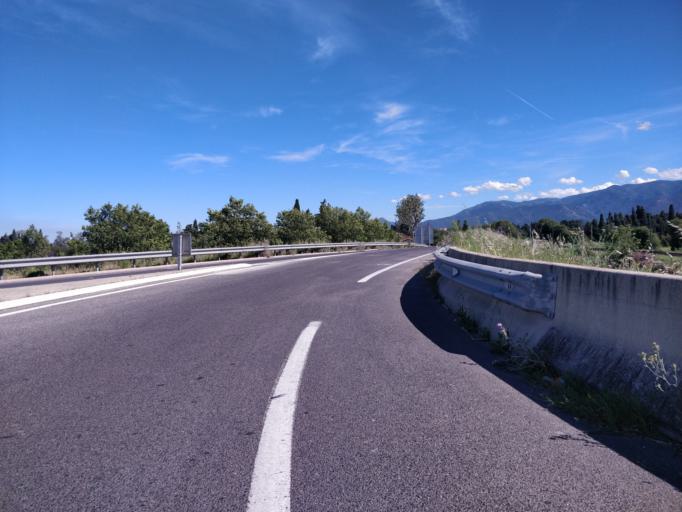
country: FR
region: Languedoc-Roussillon
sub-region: Departement des Pyrenees-Orientales
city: Corneilla-del-Vercol
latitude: 42.6156
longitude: 2.9573
